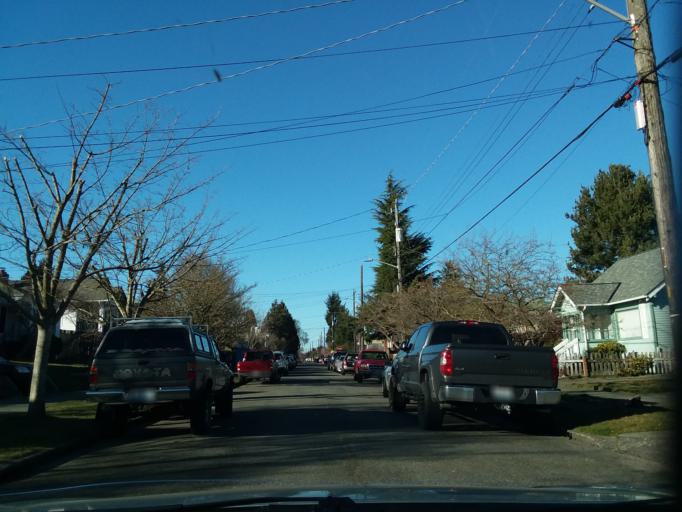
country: US
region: Washington
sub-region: King County
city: Shoreline
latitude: 47.6897
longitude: -122.3673
